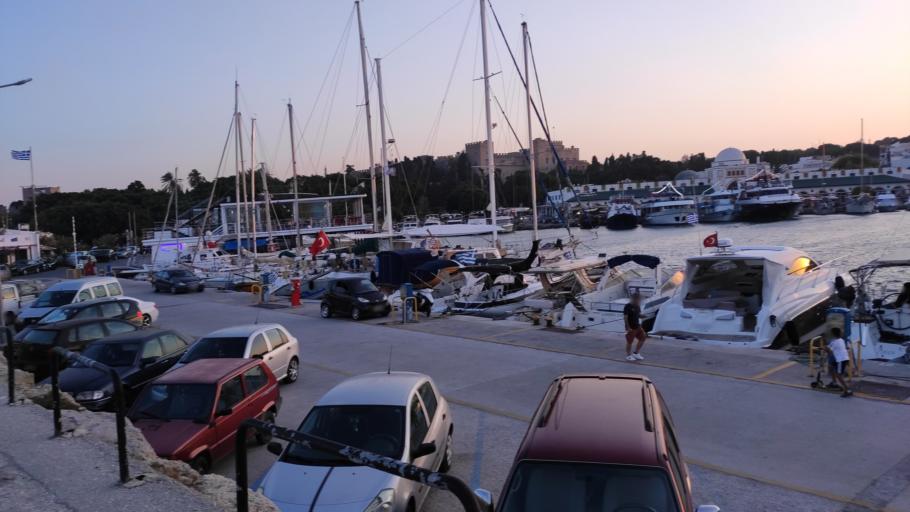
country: GR
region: South Aegean
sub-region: Nomos Dodekanisou
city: Rodos
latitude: 36.4487
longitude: 28.2278
